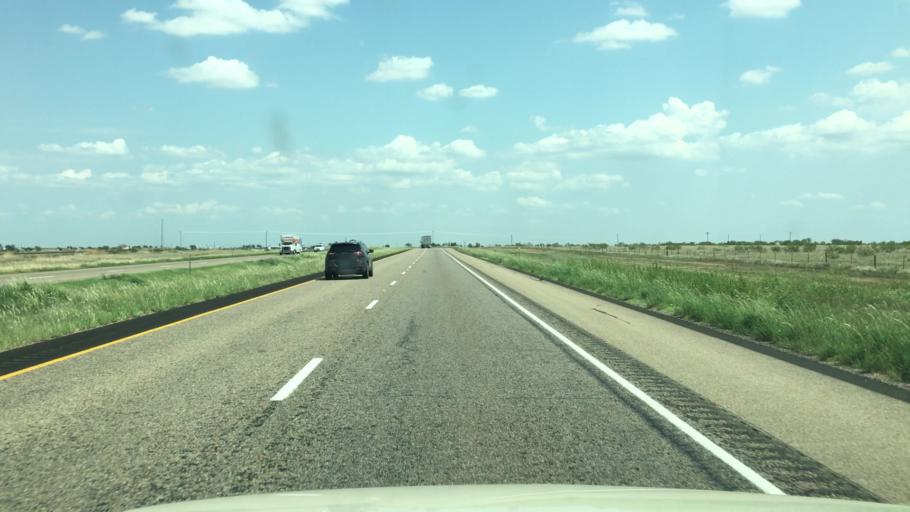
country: US
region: Texas
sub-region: Armstrong County
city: Claude
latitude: 35.0357
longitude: -101.2005
